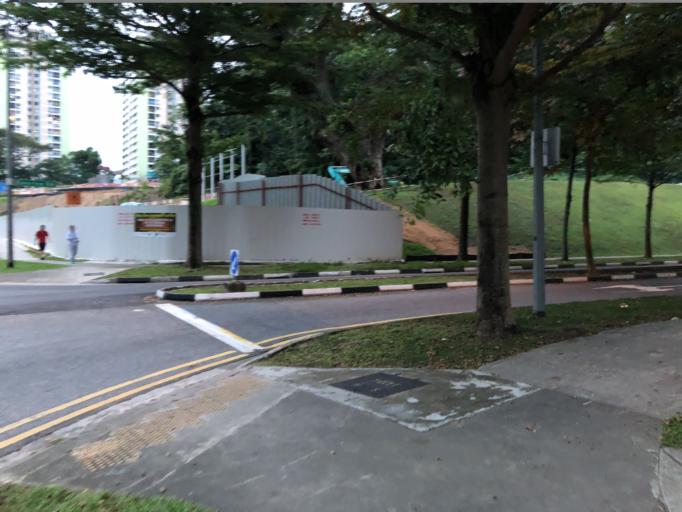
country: SG
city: Singapore
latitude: 1.2736
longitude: 103.8387
